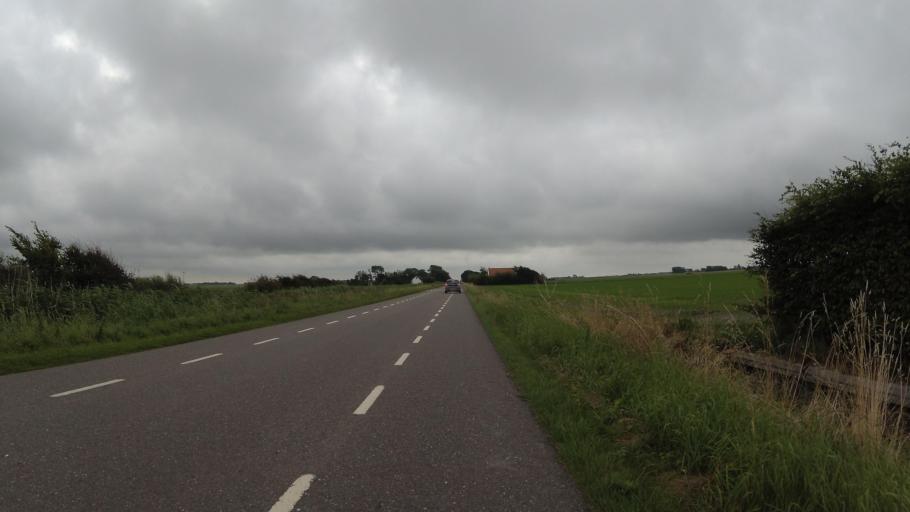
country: NL
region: North Holland
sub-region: Gemeente Den Helder
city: Den Helder
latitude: 52.8696
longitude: 4.7483
